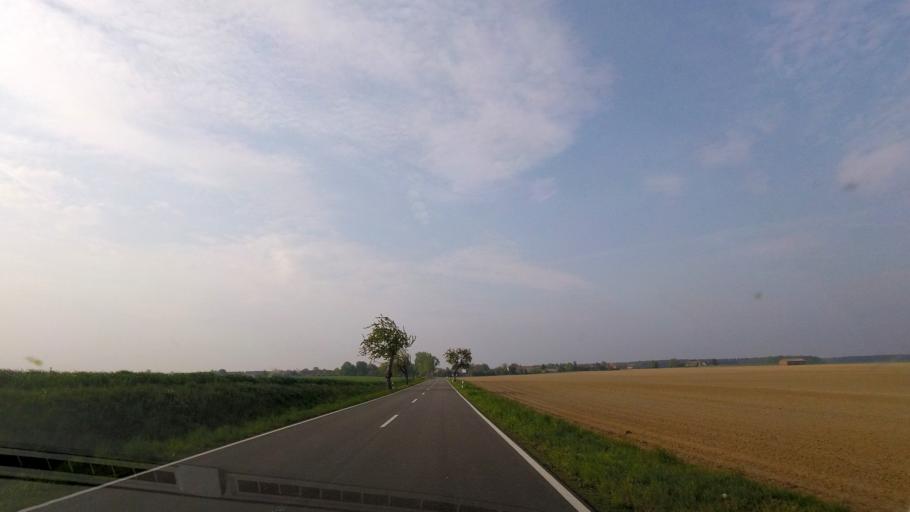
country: DE
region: Brandenburg
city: Niedergorsdorf
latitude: 51.9362
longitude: 13.0360
